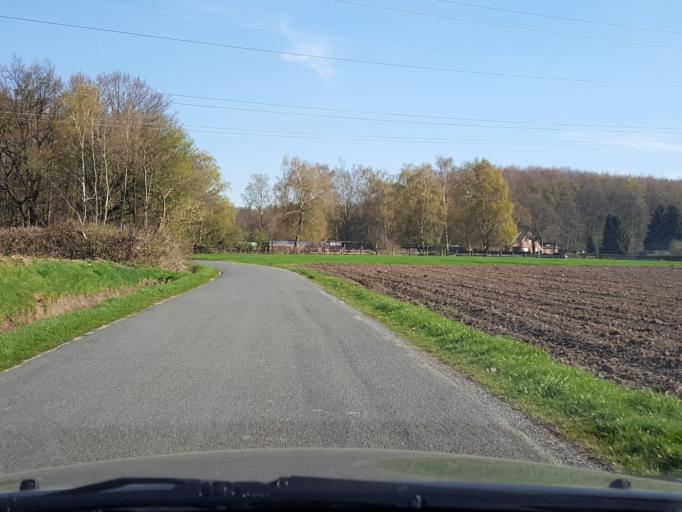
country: DE
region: North Rhine-Westphalia
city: Oer-Erkenschwick
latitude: 51.6550
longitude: 7.2336
